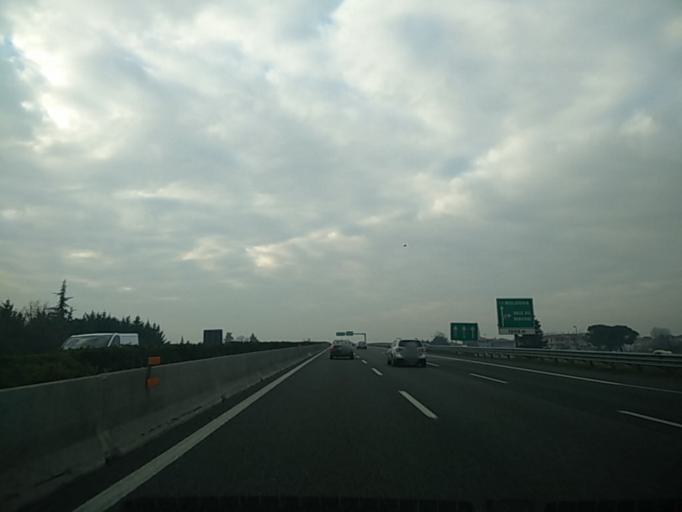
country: IT
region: Emilia-Romagna
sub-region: Forli-Cesena
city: Gatteo-Sant'Angelo
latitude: 44.1173
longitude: 12.4051
